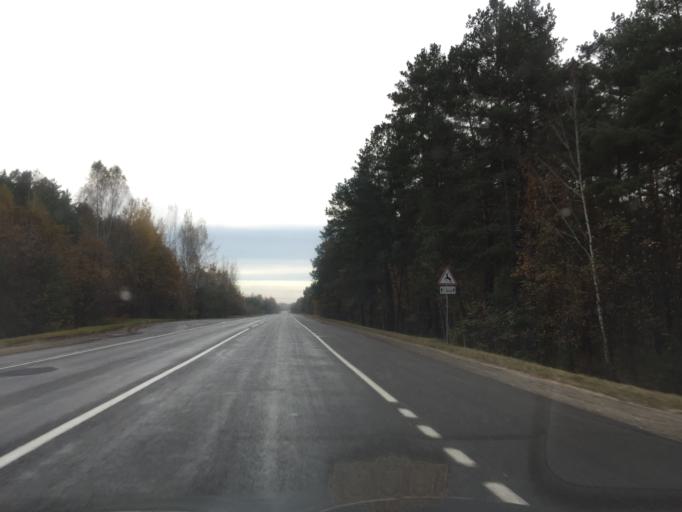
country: BY
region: Gomel
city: Kastsyukowka
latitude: 52.4312
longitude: 30.8273
